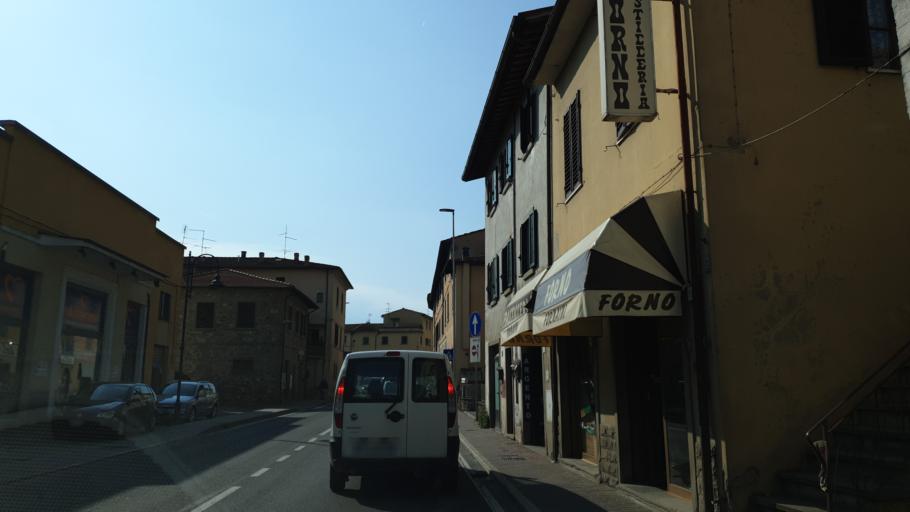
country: IT
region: Tuscany
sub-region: Province of Arezzo
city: Ponte a Poppi
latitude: 43.7280
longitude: 11.7697
